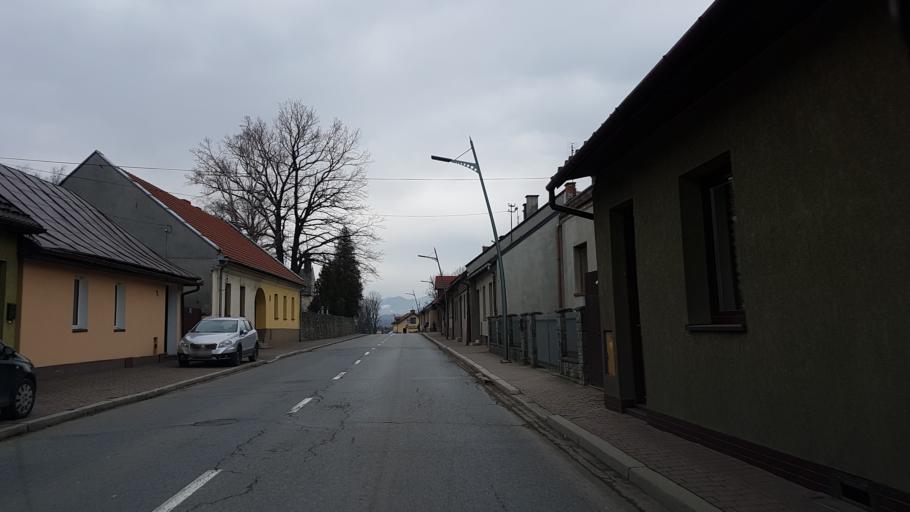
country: PL
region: Lesser Poland Voivodeship
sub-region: Powiat nowosadecki
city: Stary Sacz
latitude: 49.5582
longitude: 20.6375
